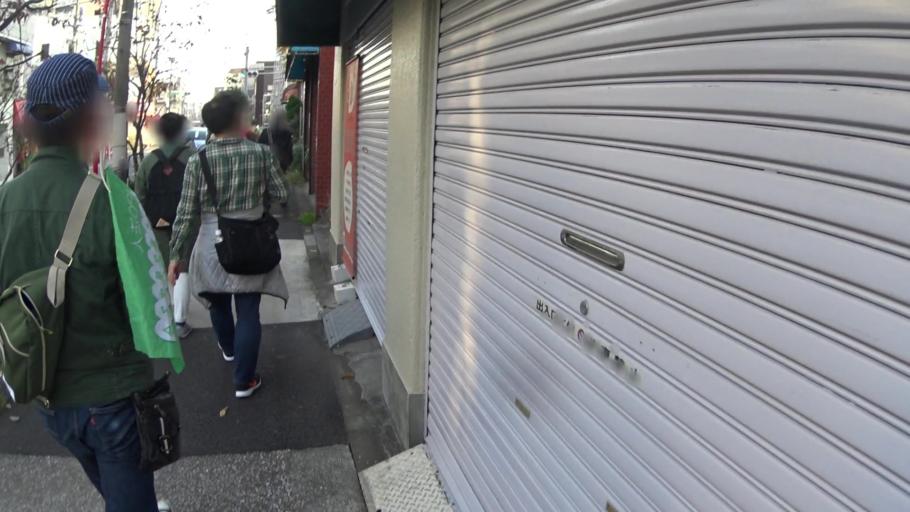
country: JP
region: Tokyo
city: Urayasu
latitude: 35.7126
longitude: 139.8161
